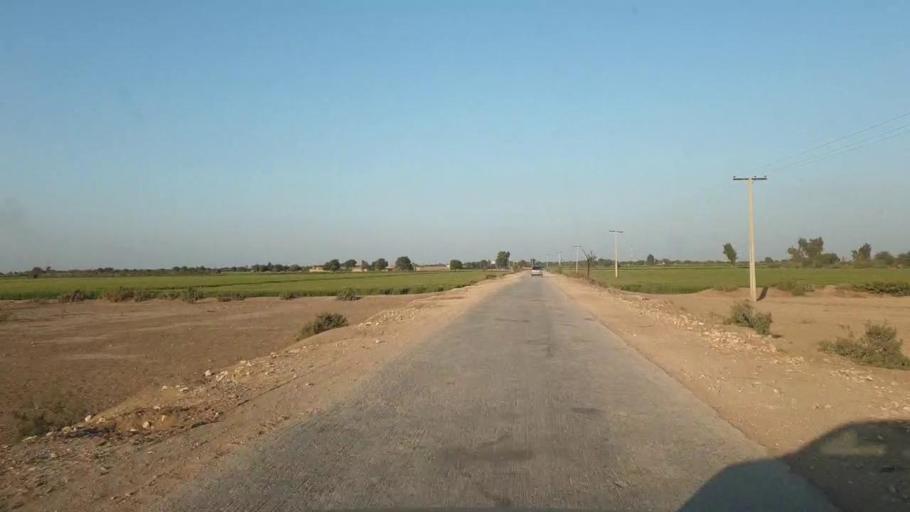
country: PK
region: Sindh
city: Tando Allahyar
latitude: 25.3823
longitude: 68.7525
